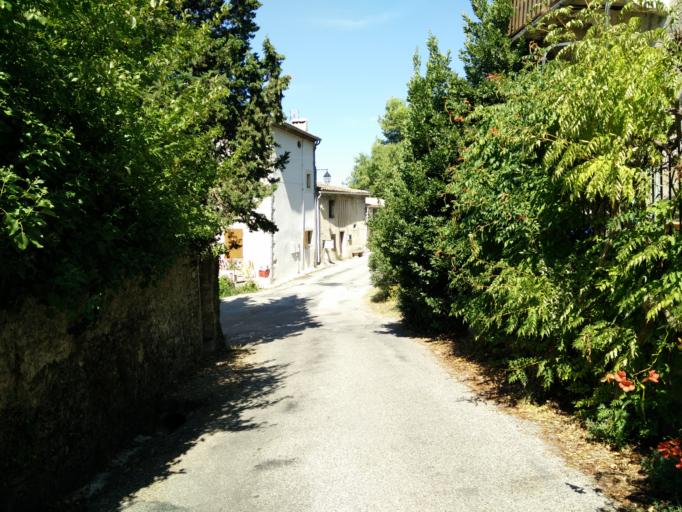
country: FR
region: Rhone-Alpes
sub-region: Departement de la Drome
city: La Begude-de-Mazenc
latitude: 44.5509
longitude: 4.9375
